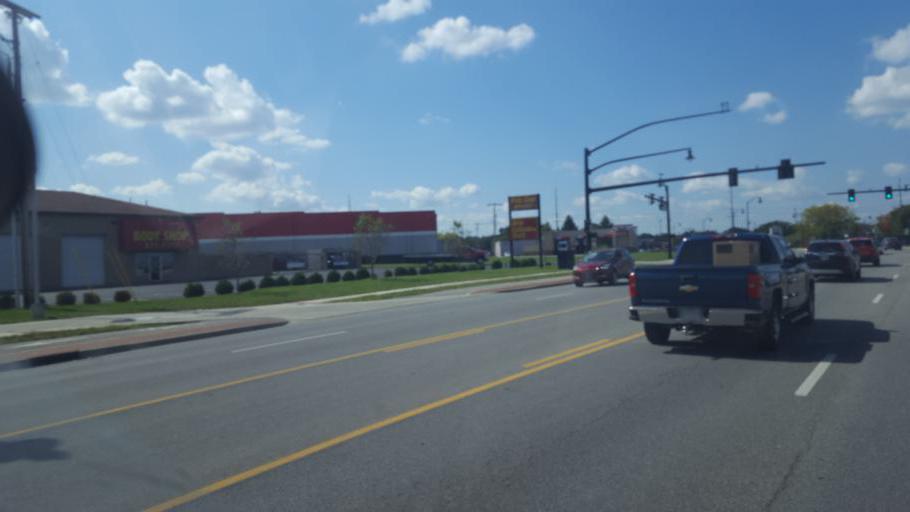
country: US
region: Ohio
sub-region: Franklin County
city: Grove City
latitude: 39.8803
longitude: -83.0662
